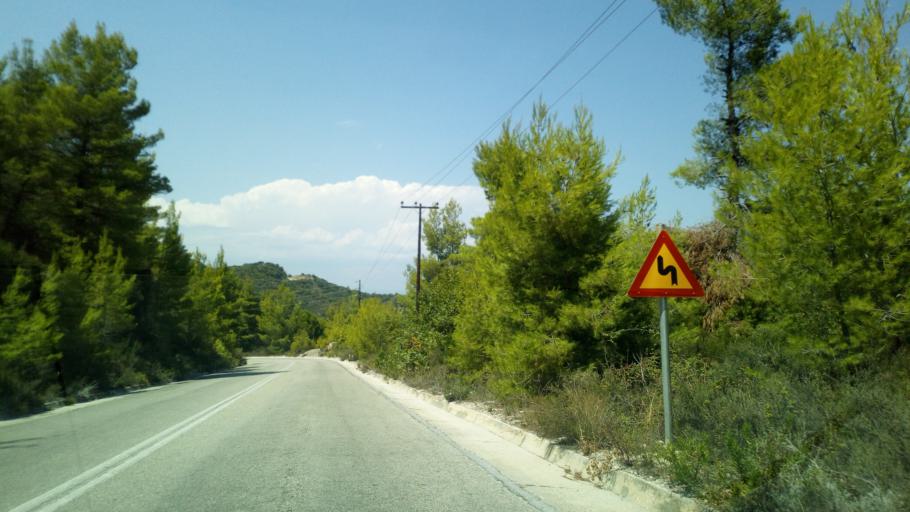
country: GR
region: Central Macedonia
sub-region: Nomos Chalkidikis
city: Sarti
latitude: 40.1498
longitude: 23.9194
